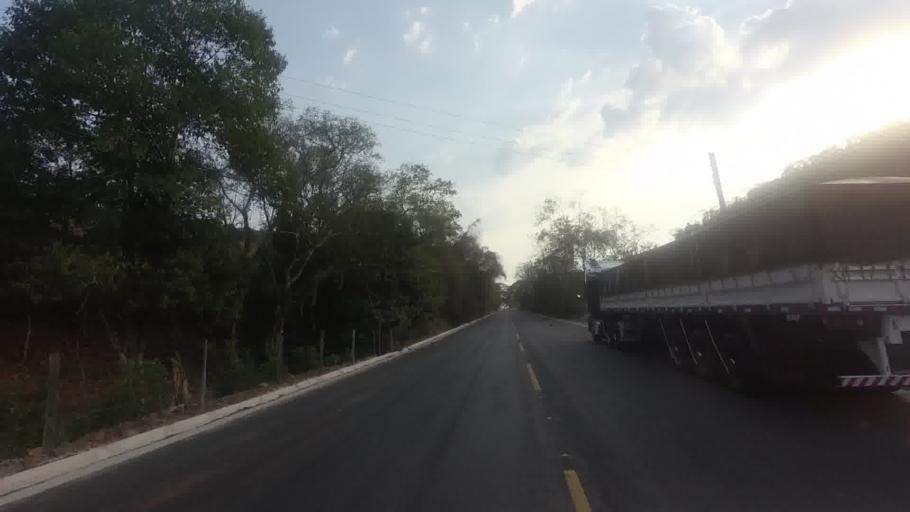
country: BR
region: Rio de Janeiro
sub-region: Cambuci
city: Cambuci
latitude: -21.4299
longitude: -42.0021
